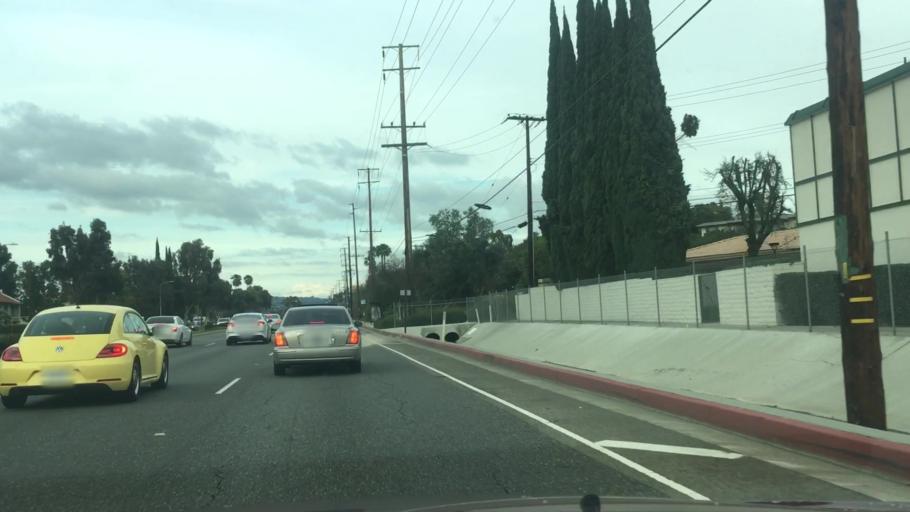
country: US
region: California
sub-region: Orange County
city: Buena Park
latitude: 33.8922
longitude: -117.9900
